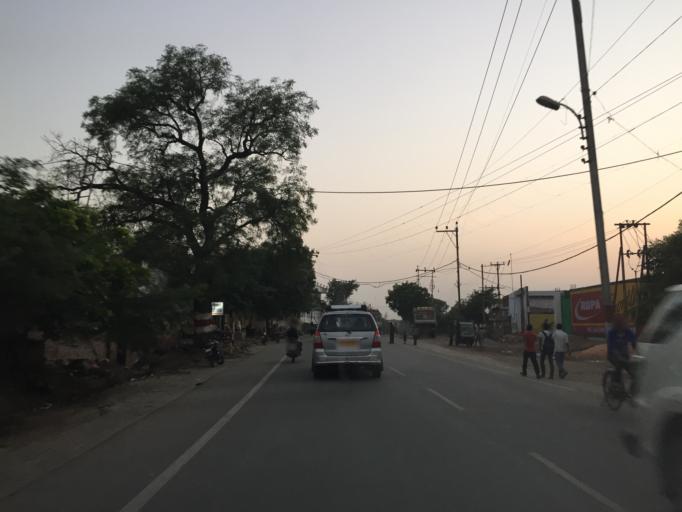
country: IN
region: Uttar Pradesh
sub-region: Agra
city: Dayal Bagh
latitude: 27.2069
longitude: 78.0616
